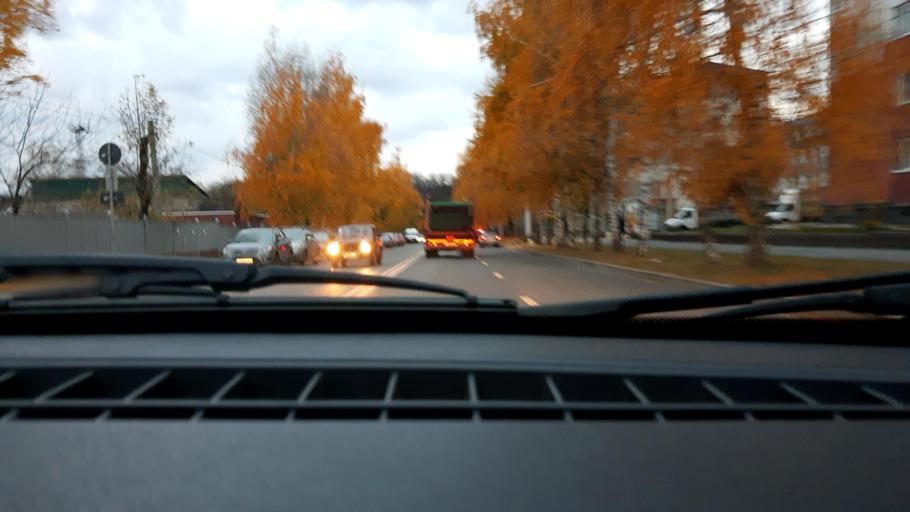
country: RU
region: Bashkortostan
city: Ufa
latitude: 54.7652
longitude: 56.0126
